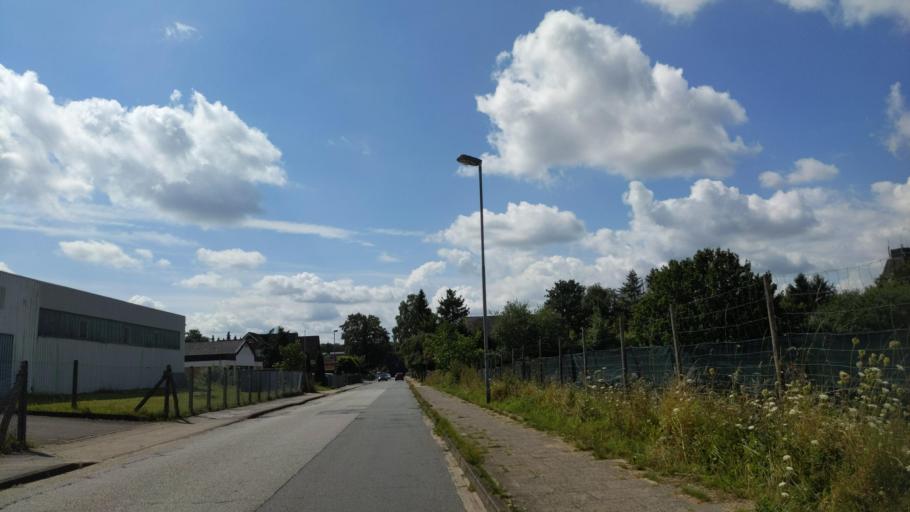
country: DE
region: Schleswig-Holstein
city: Reinfeld
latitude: 53.8312
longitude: 10.4989
